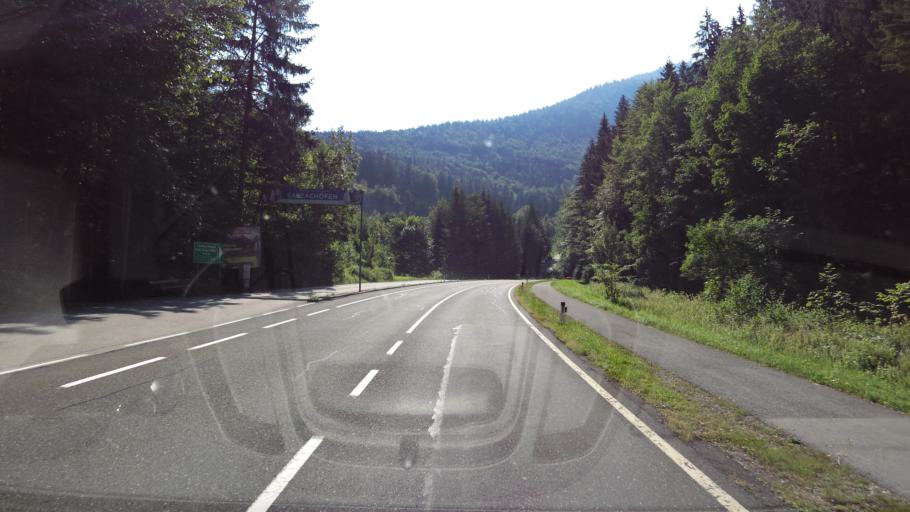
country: AT
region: Salzburg
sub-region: Politischer Bezirk Hallein
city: Scheffau am Tennengebirge
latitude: 47.5780
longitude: 13.1928
